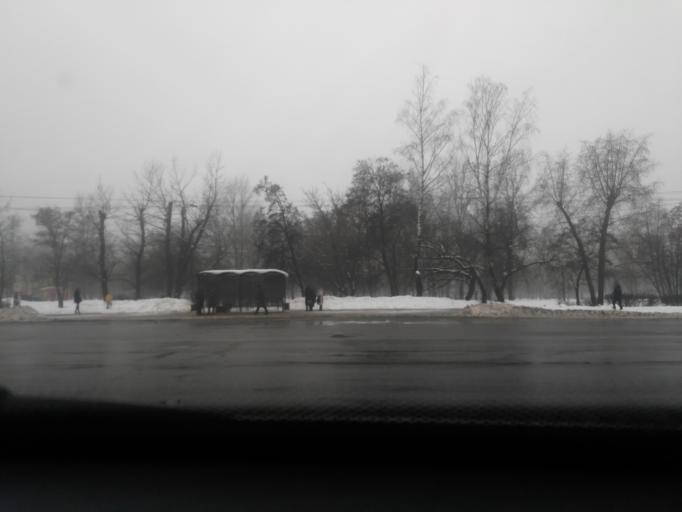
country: BY
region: Mogilev
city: Babruysk
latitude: 53.1679
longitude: 29.2074
